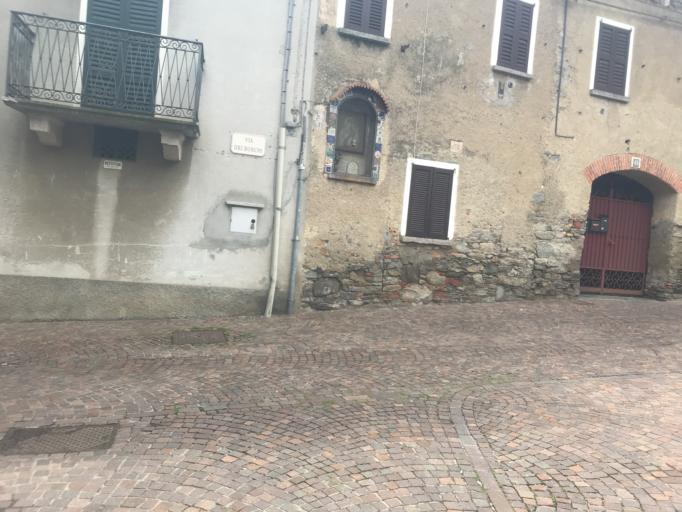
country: IT
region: Piedmont
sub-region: Provincia di Novara
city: Pisano
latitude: 45.8030
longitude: 8.5159
